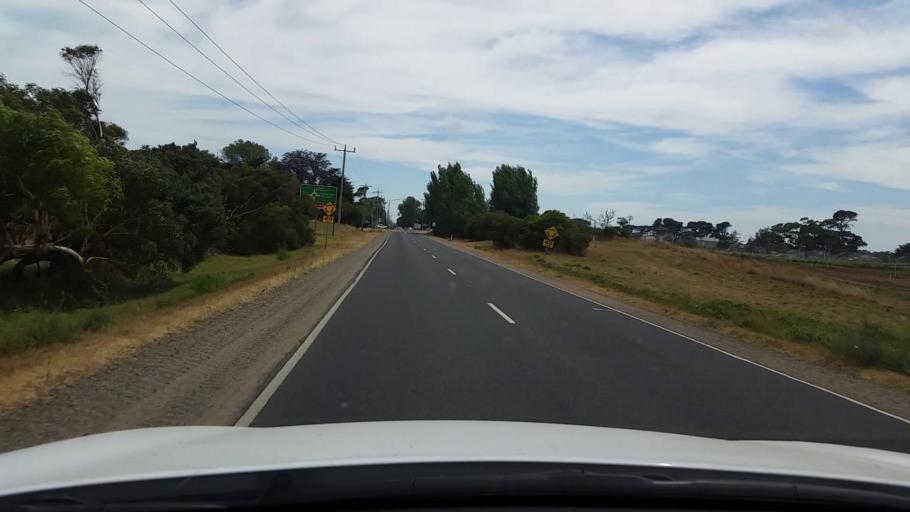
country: AU
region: Victoria
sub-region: Mornington Peninsula
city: Rosebud West
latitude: -38.4005
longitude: 144.8880
